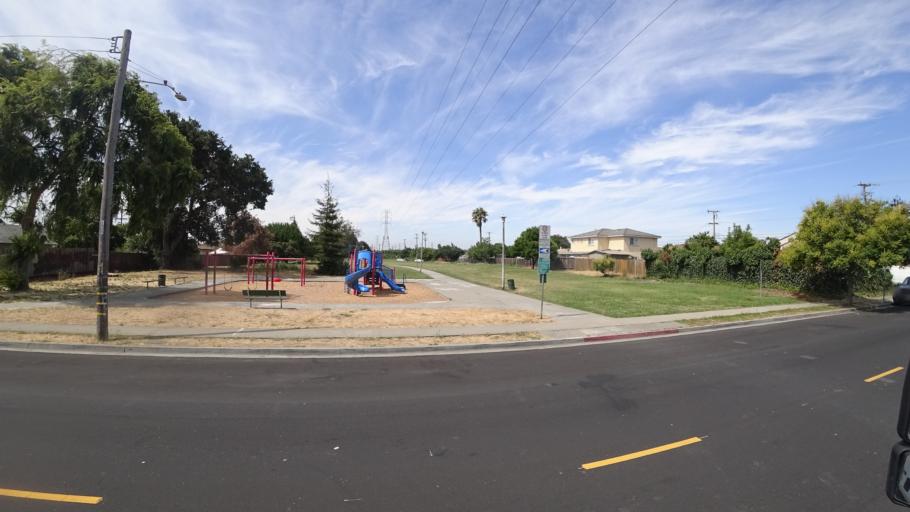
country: US
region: California
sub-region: Alameda County
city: Hayward
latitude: 37.6428
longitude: -122.0893
